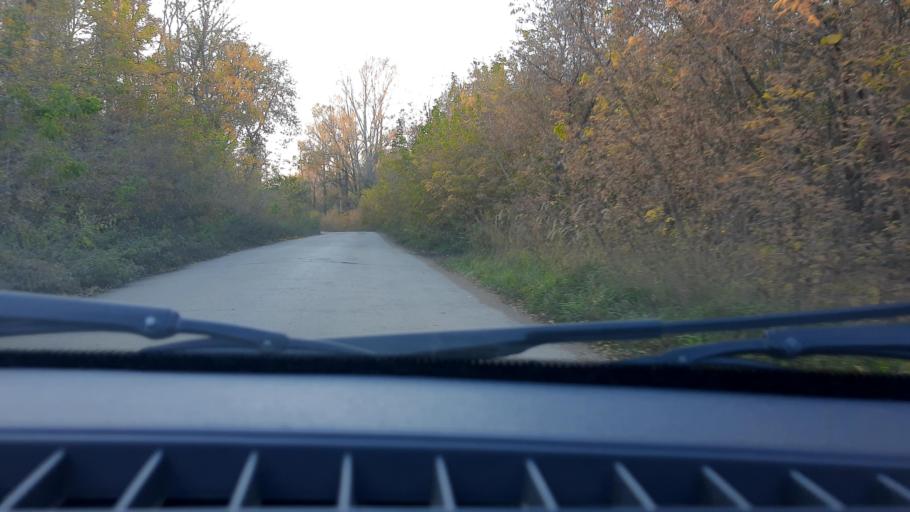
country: RU
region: Bashkortostan
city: Ufa
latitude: 54.7984
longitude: 56.1767
